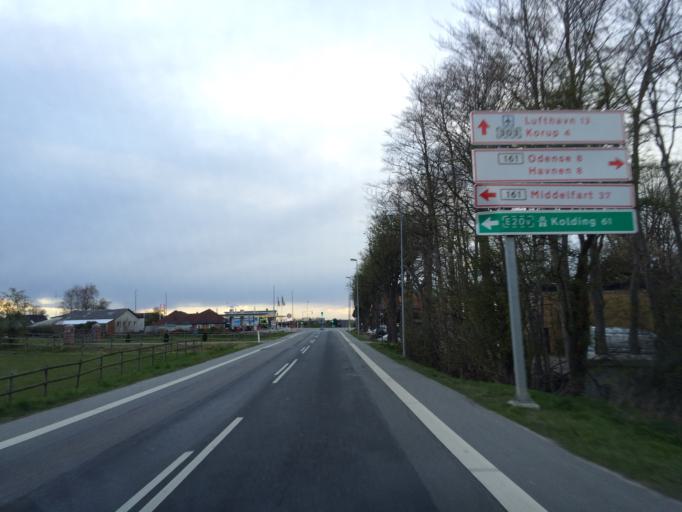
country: DK
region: South Denmark
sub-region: Odense Kommune
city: Bellinge
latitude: 55.3884
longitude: 10.2624
